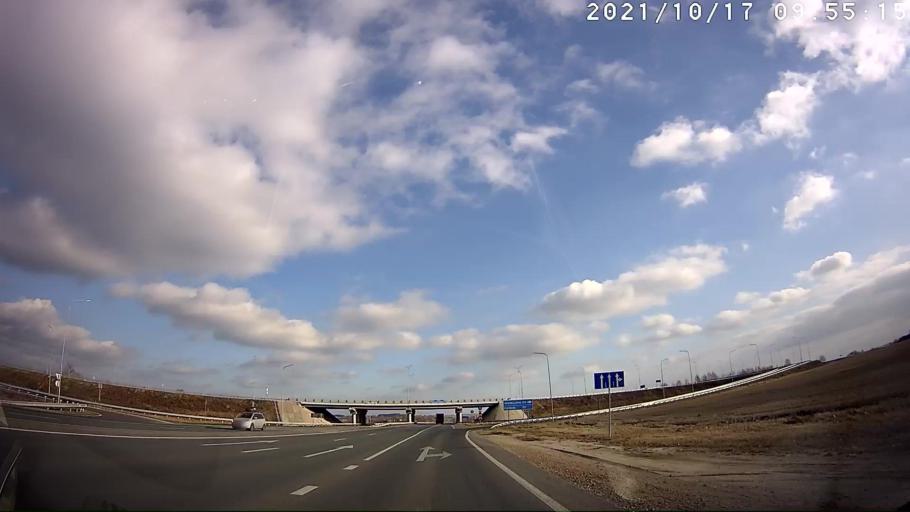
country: RU
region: Mariy-El
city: Yoshkar-Ola
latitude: 56.6785
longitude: 48.0209
